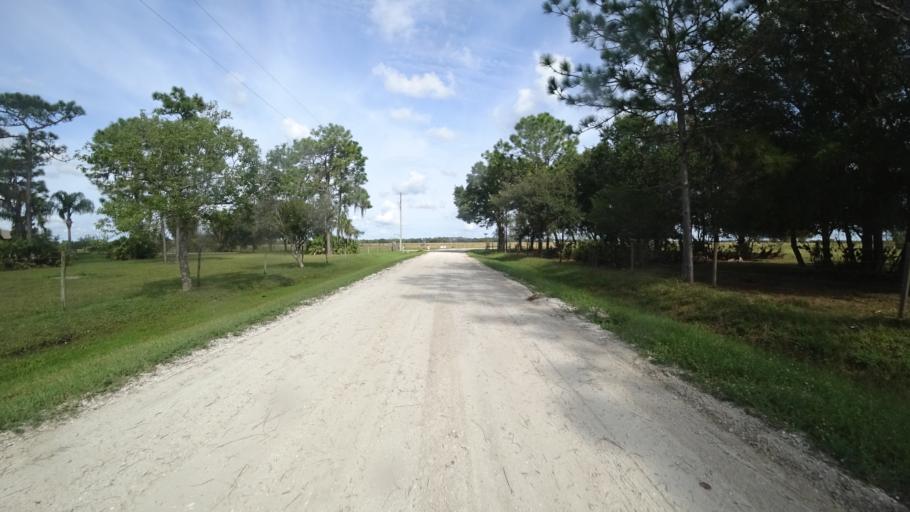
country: US
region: Florida
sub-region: Sarasota County
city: The Meadows
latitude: 27.4157
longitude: -82.2996
